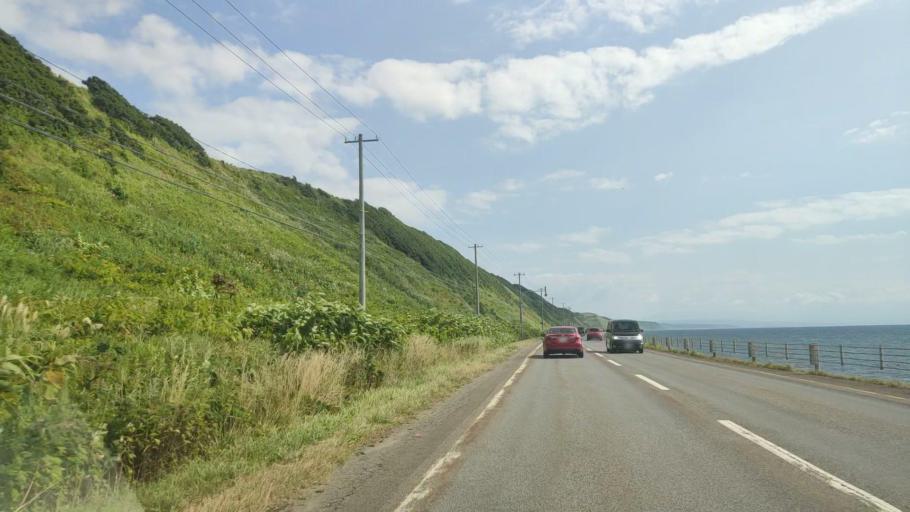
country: JP
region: Hokkaido
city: Rumoi
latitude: 44.0907
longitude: 141.6610
